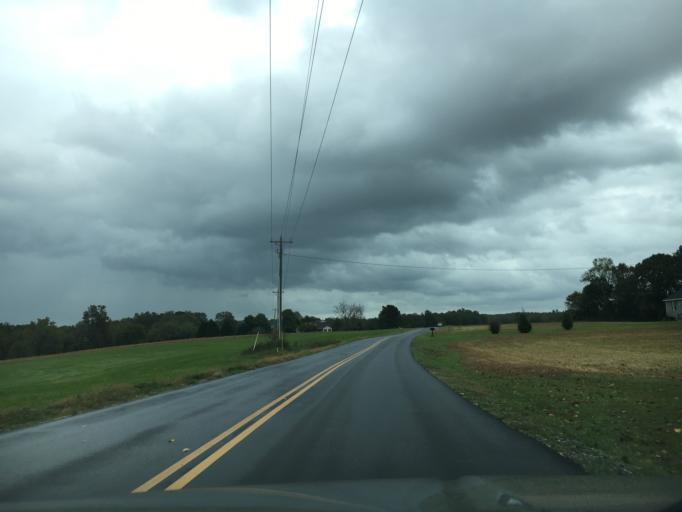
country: US
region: Virginia
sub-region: Amelia County
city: Amelia Court House
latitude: 37.4075
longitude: -77.9651
